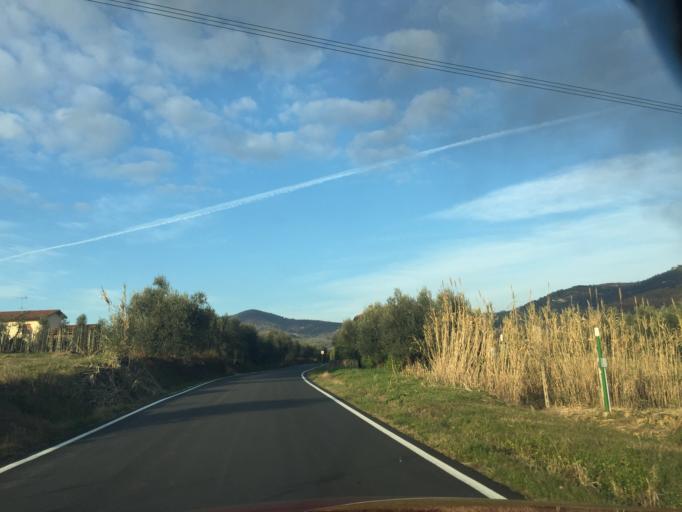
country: IT
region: Tuscany
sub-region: Provincia di Pistoia
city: San Rocco
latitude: 43.8350
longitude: 10.8664
